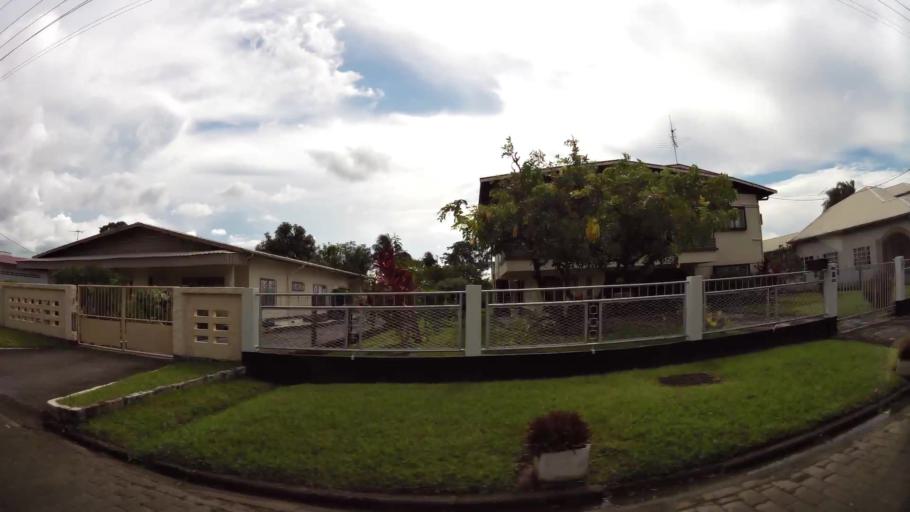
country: SR
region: Paramaribo
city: Paramaribo
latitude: 5.8435
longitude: -55.1911
